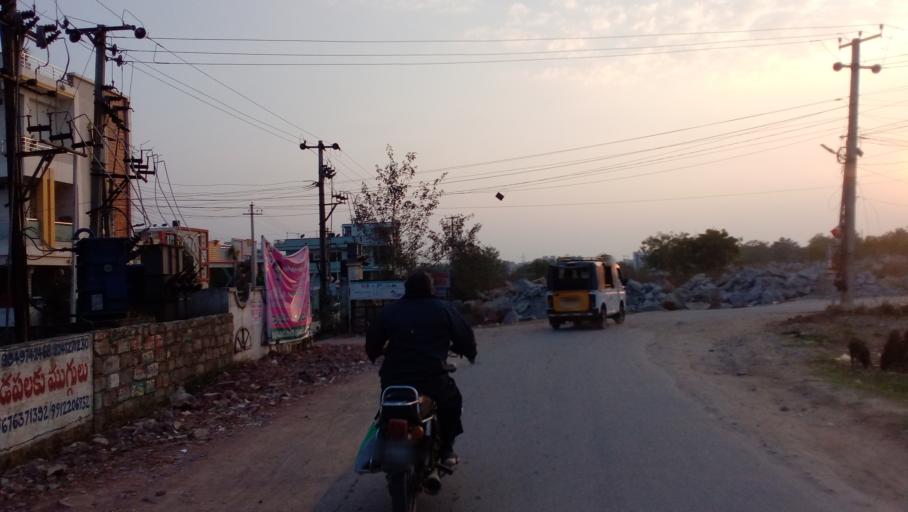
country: IN
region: Telangana
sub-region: Medak
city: Serilingampalle
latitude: 17.5186
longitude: 78.3133
